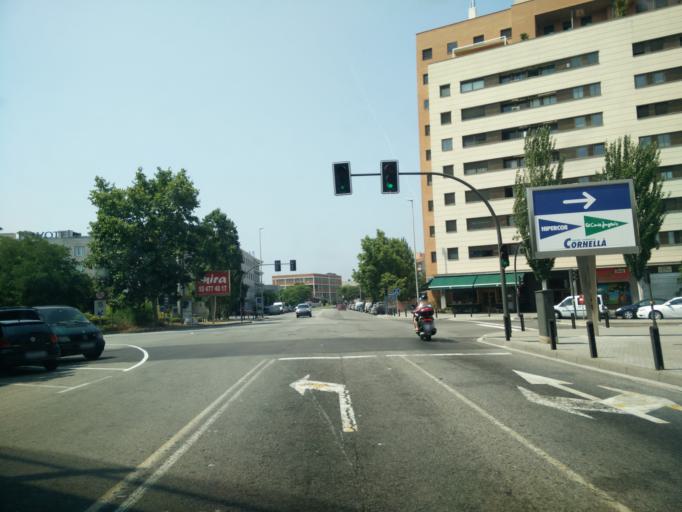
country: ES
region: Catalonia
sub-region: Provincia de Barcelona
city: Cornella de Llobregat
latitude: 41.3527
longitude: 2.0912
